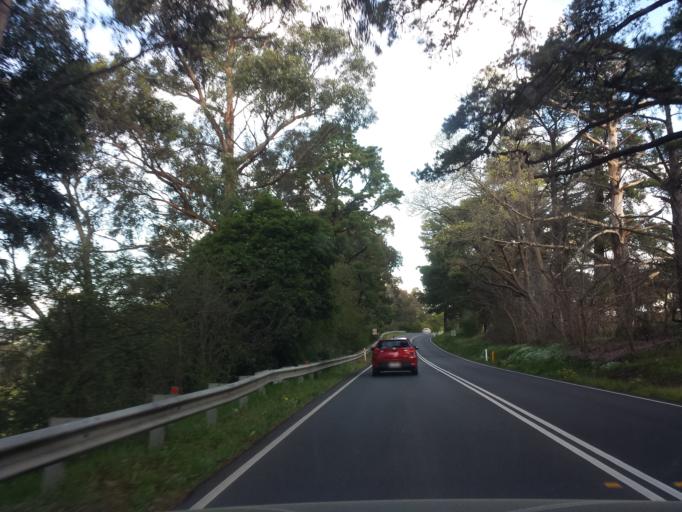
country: AU
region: Victoria
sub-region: Casey
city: Berwick
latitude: -38.0064
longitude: 145.3432
